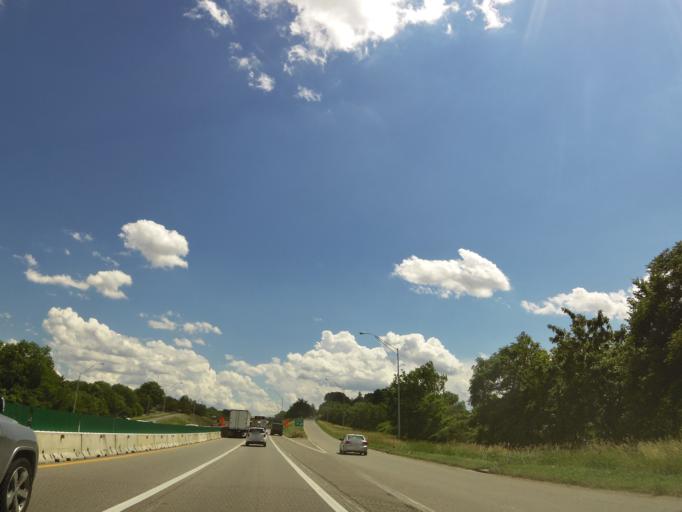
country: US
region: Iowa
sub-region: Linn County
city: Cedar Rapids
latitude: 41.9606
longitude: -91.6710
